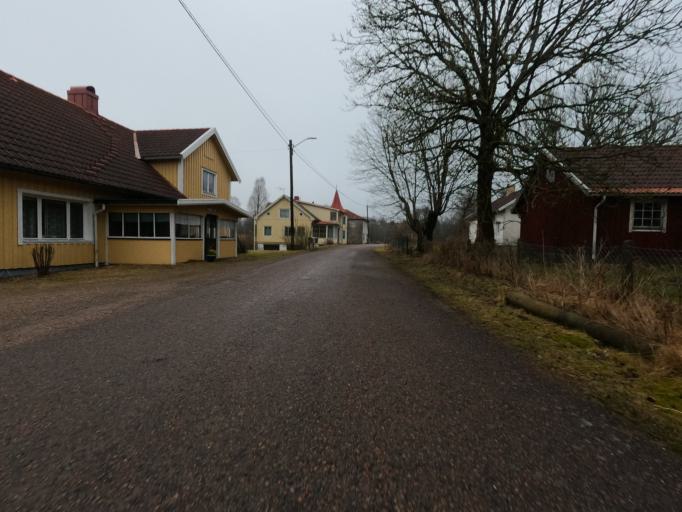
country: SE
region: Halland
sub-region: Hylte Kommun
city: Hyltebruk
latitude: 56.8087
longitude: 13.2680
